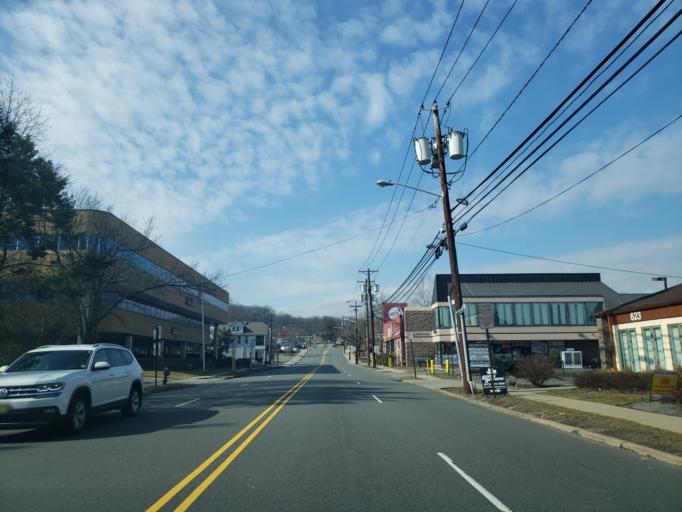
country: US
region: New Jersey
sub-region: Essex County
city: West Orange
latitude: 40.8098
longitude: -74.2572
